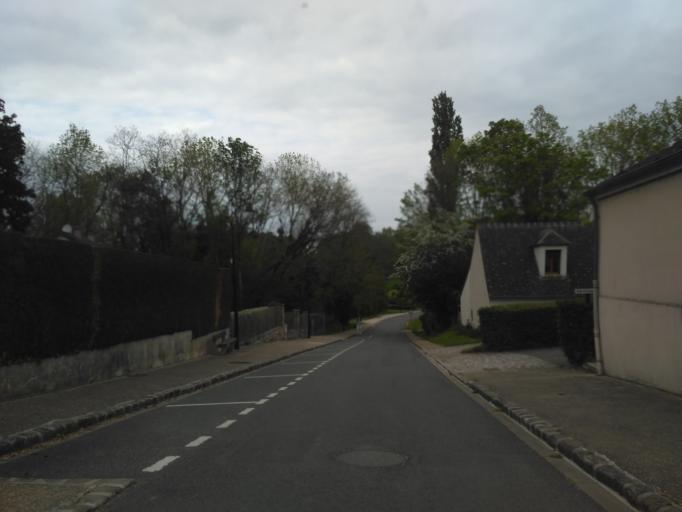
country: FR
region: Ile-de-France
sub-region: Departement de Seine-et-Marne
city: Moisenay
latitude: 48.5693
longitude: 2.7815
